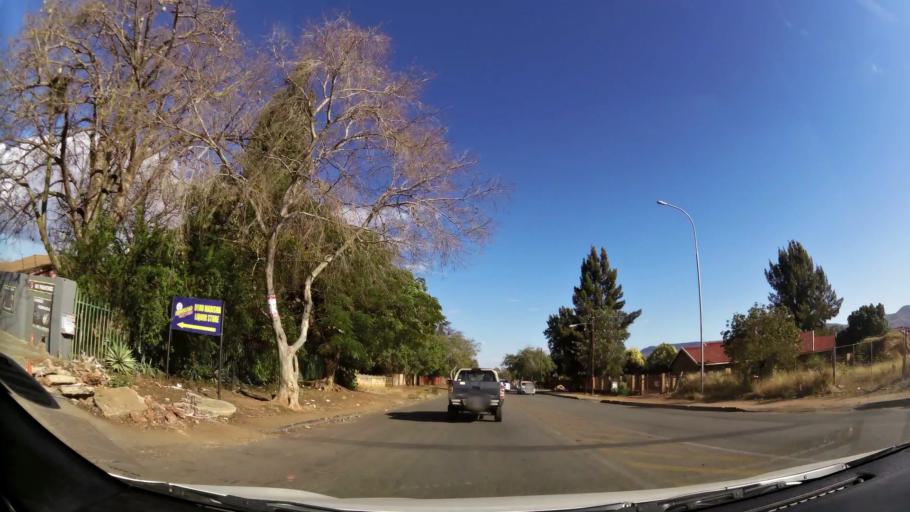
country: ZA
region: Limpopo
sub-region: Waterberg District Municipality
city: Mokopane
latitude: -24.1779
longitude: 29.0016
